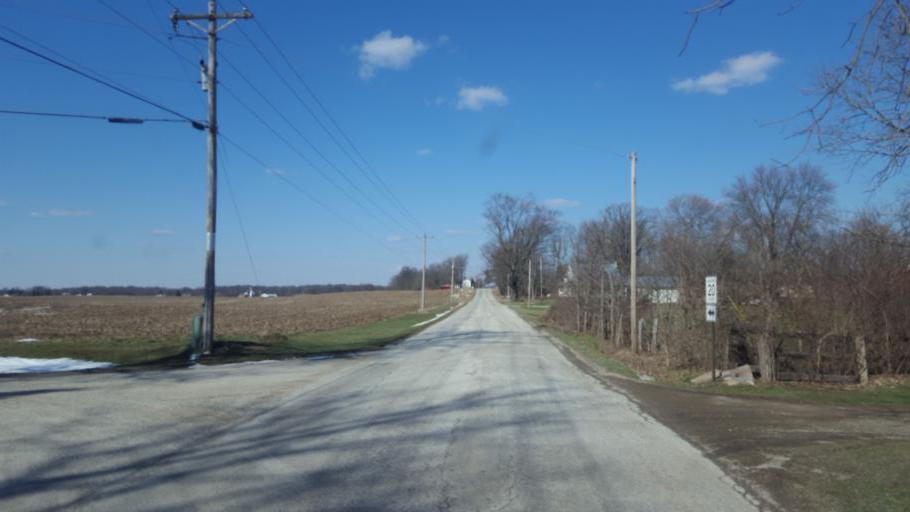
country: US
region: Ohio
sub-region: Morrow County
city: Mount Gilead
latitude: 40.4821
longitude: -82.7541
